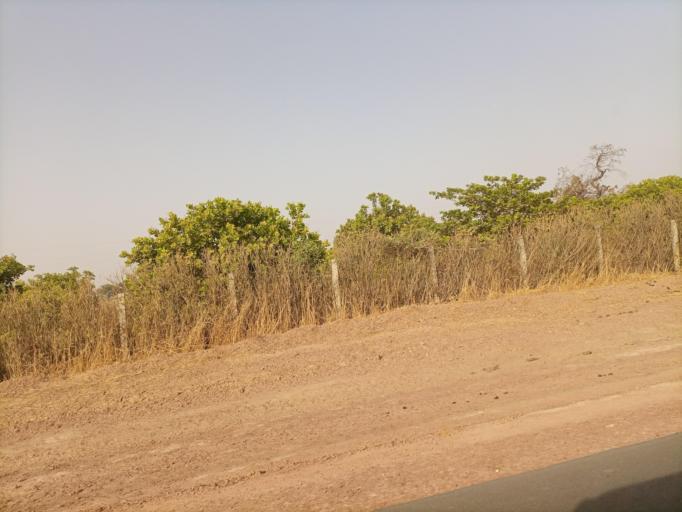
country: SN
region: Fatick
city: Passi
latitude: 14.0301
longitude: -16.3093
